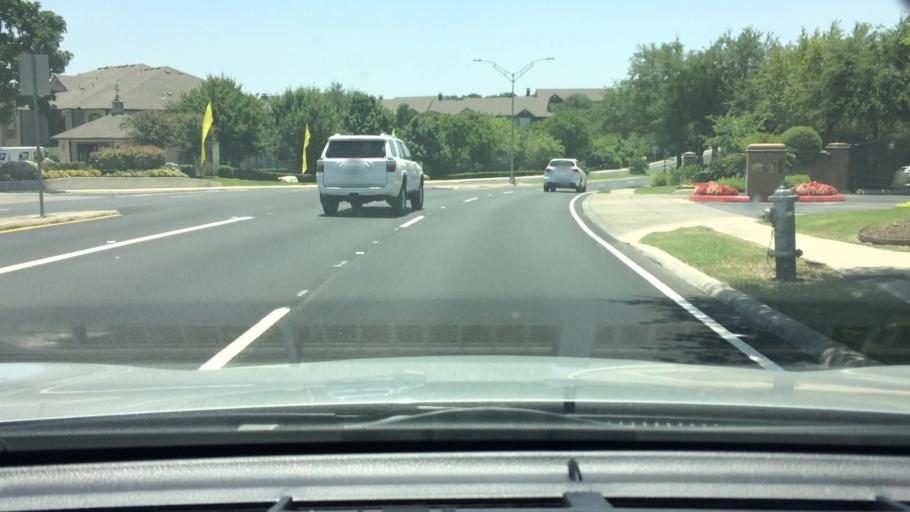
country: US
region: Texas
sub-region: Bexar County
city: Shavano Park
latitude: 29.5578
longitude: -98.5747
